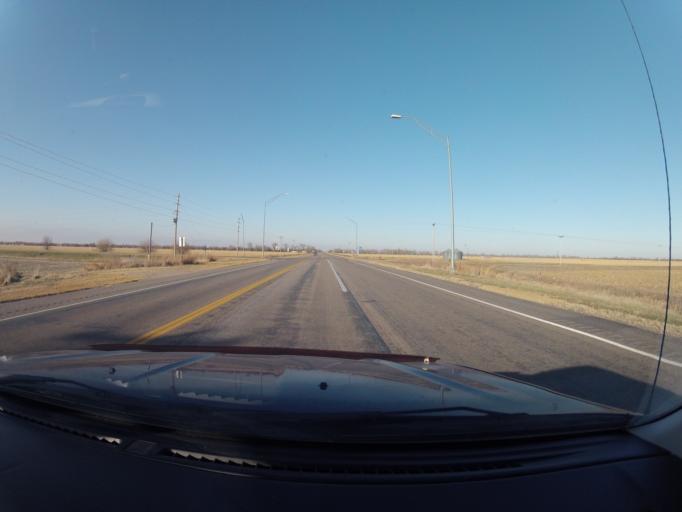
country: US
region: Nebraska
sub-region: Kearney County
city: Minden
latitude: 40.6403
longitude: -98.9514
